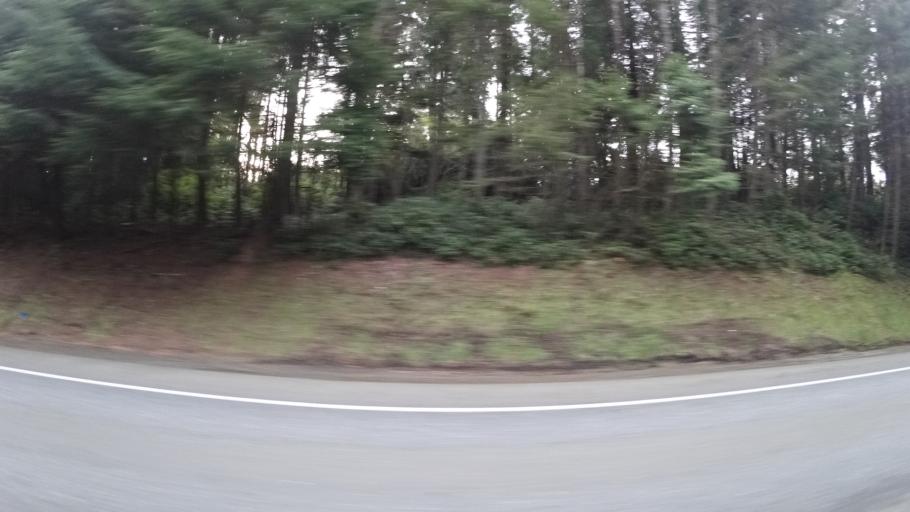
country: US
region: Oregon
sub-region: Coos County
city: Lakeside
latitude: 43.5474
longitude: -124.2113
